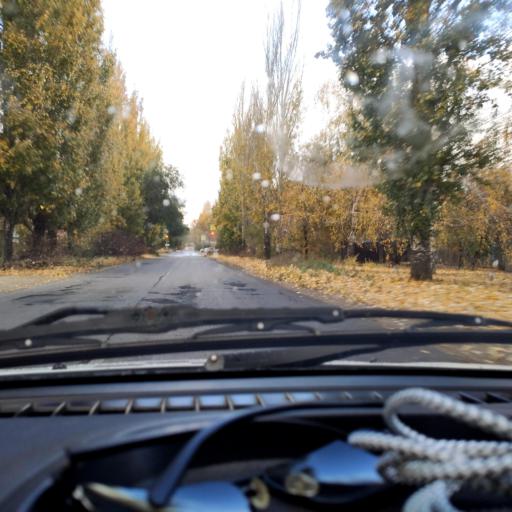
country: RU
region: Samara
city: Tol'yatti
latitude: 53.5351
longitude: 49.4174
